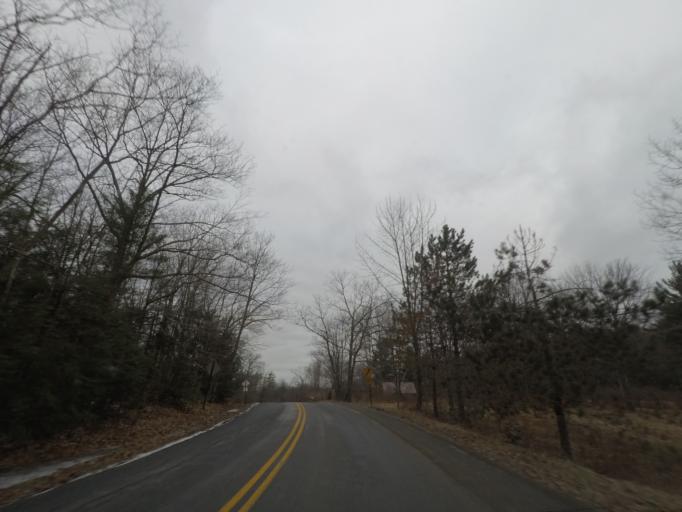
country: US
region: New York
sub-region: Rensselaer County
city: Poestenkill
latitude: 42.7321
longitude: -73.5049
